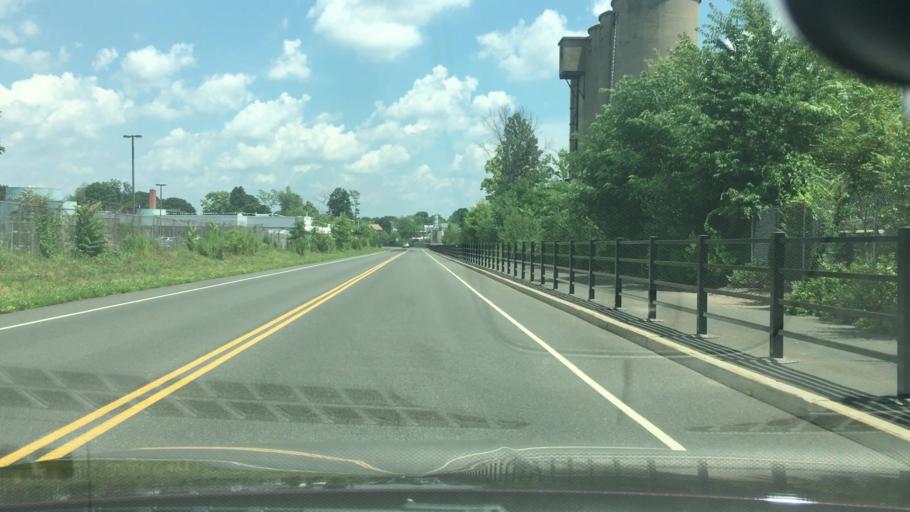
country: US
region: Connecticut
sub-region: Hartford County
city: New Britain
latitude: 41.6693
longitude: -72.7708
